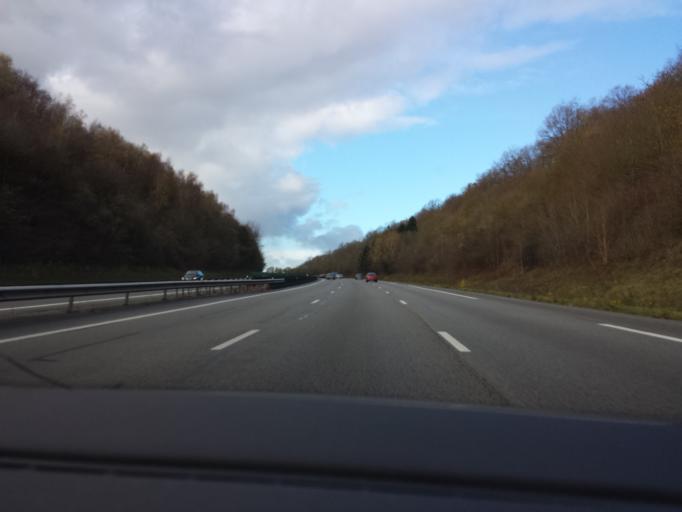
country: FR
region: Ile-de-France
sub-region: Departement des Yvelines
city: Bonnieres-sur-Seine
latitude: 49.0184
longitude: 1.5821
